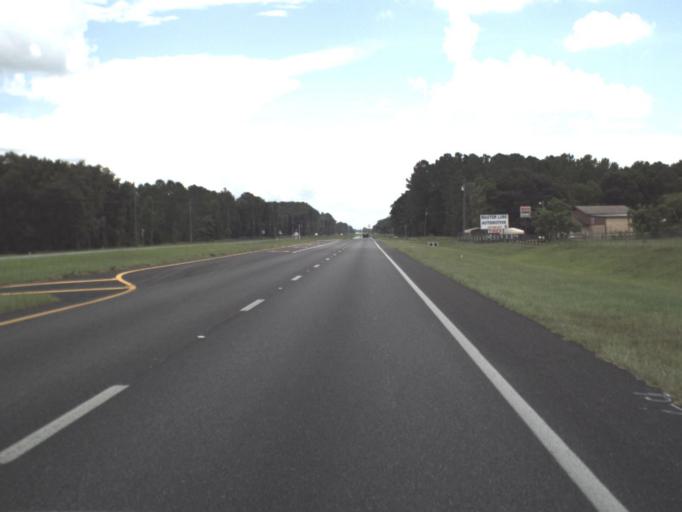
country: US
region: Florida
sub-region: Levy County
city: Williston
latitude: 29.3964
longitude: -82.4921
